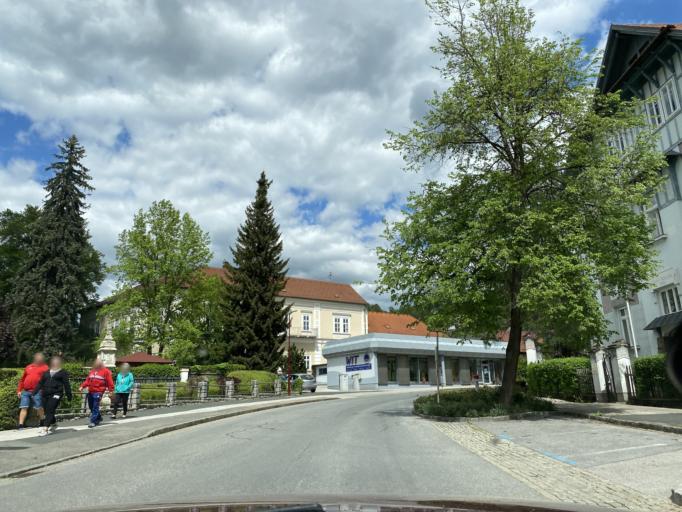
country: AT
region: Carinthia
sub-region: Politischer Bezirk Wolfsberg
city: Wolfsberg
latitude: 46.8362
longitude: 14.8446
